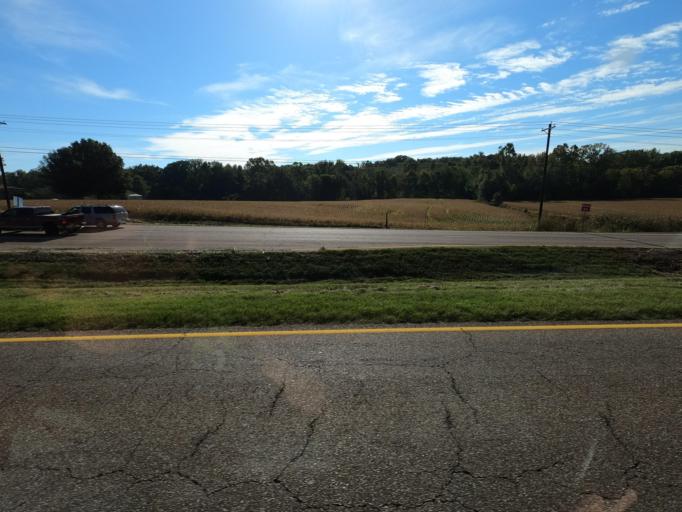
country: US
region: Tennessee
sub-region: Tipton County
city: Brighton
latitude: 35.5257
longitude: -89.6895
